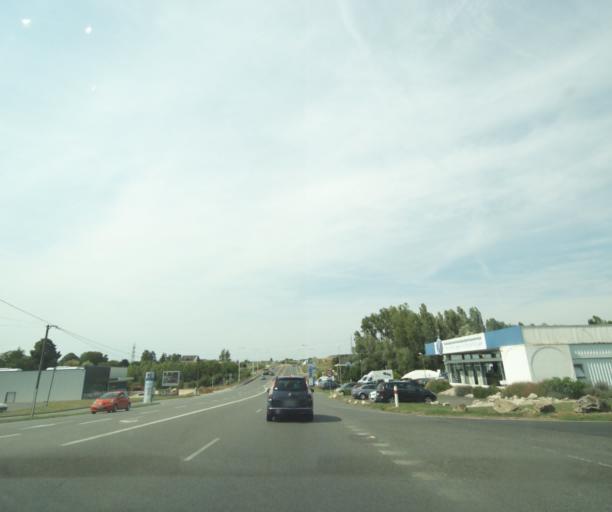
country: FR
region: Centre
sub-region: Departement d'Indre-et-Loire
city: Chambray-les-Tours
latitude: 47.3182
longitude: 0.7106
